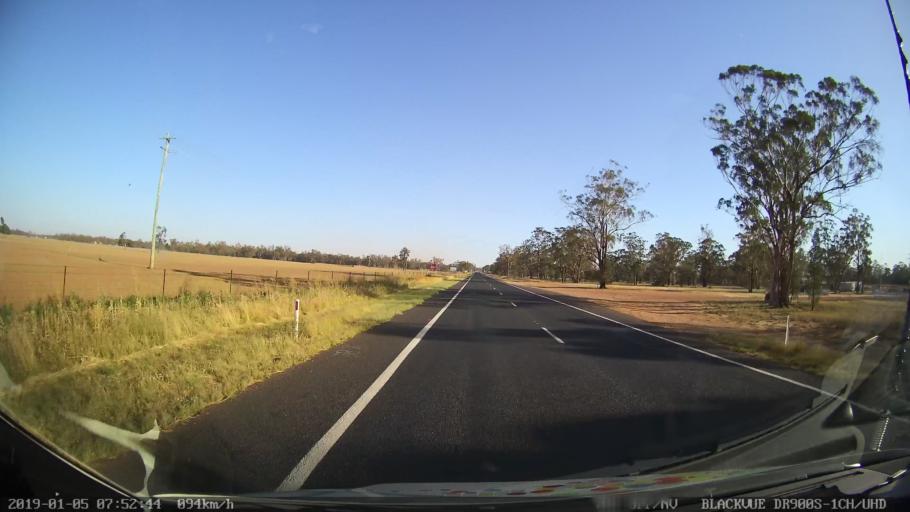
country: AU
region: New South Wales
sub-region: Gilgandra
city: Gilgandra
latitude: -31.7542
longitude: 148.6406
